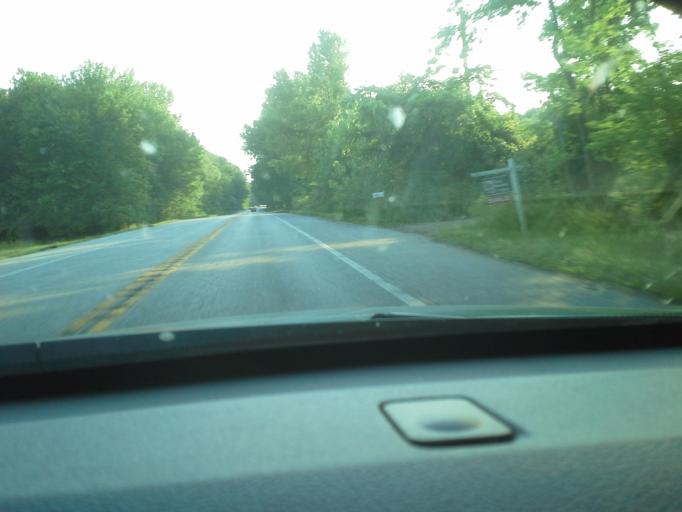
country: US
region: Maryland
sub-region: Anne Arundel County
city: Deale
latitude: 38.7873
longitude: -76.5913
